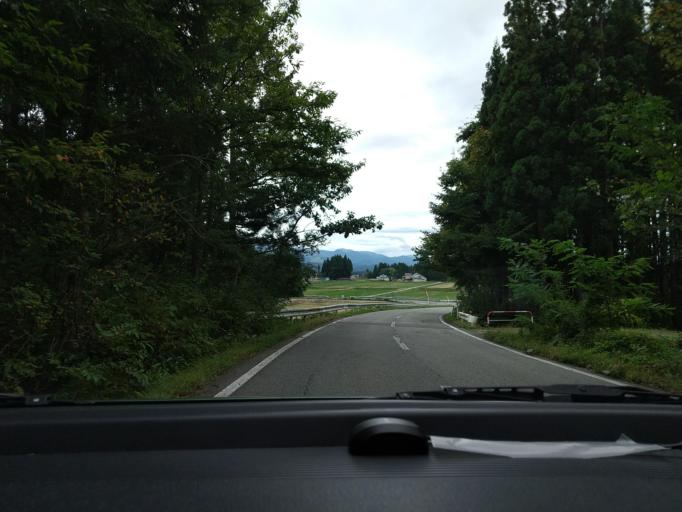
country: JP
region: Akita
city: Kakunodatemachi
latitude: 39.5477
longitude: 140.6340
